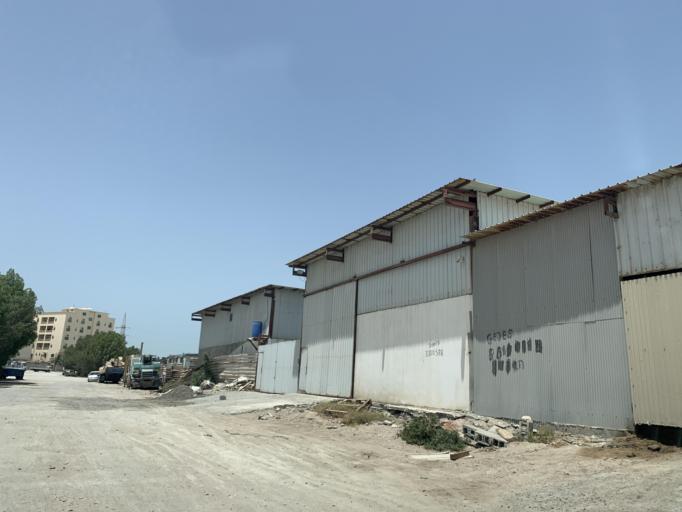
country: BH
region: Northern
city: Sitrah
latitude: 26.1739
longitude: 50.6066
